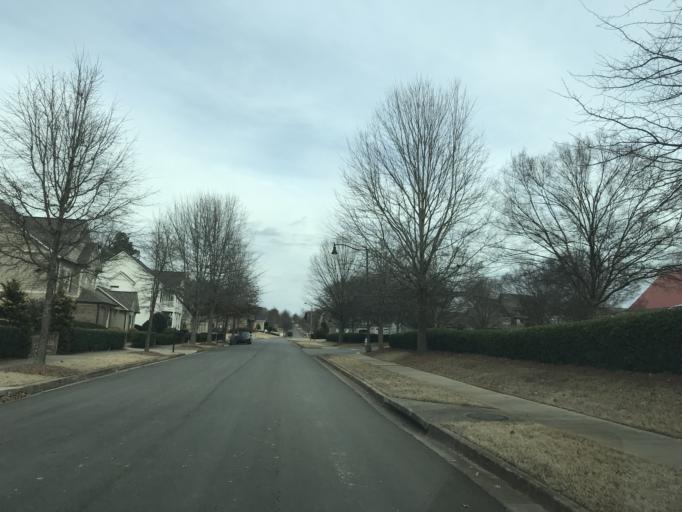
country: US
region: Georgia
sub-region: Cherokee County
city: Canton
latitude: 34.2038
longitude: -84.3999
